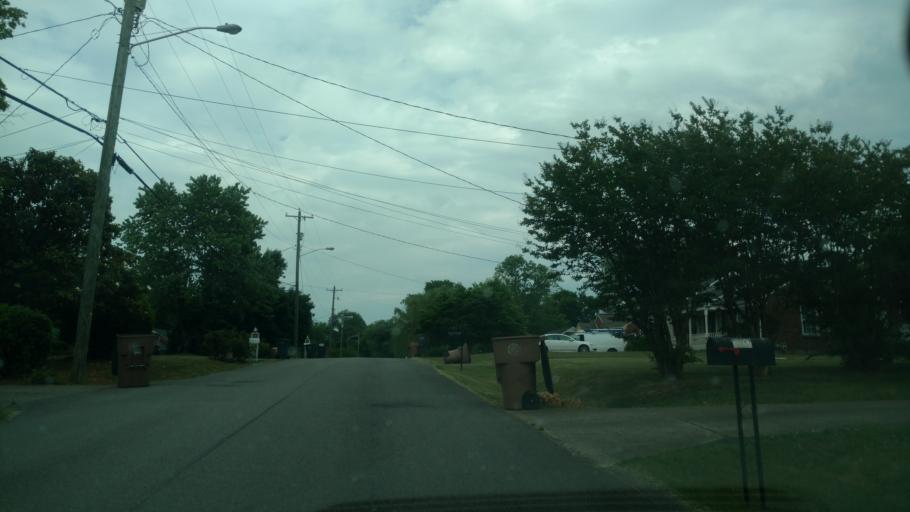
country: US
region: Tennessee
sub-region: Davidson County
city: Lakewood
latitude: 36.2112
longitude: -86.7087
